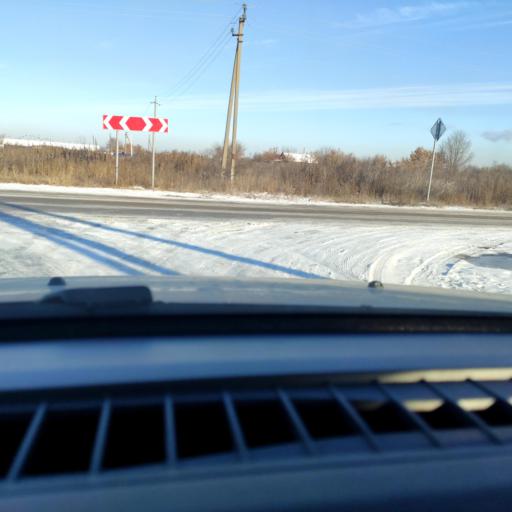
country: RU
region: Samara
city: Podstepki
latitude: 53.5189
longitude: 49.1284
